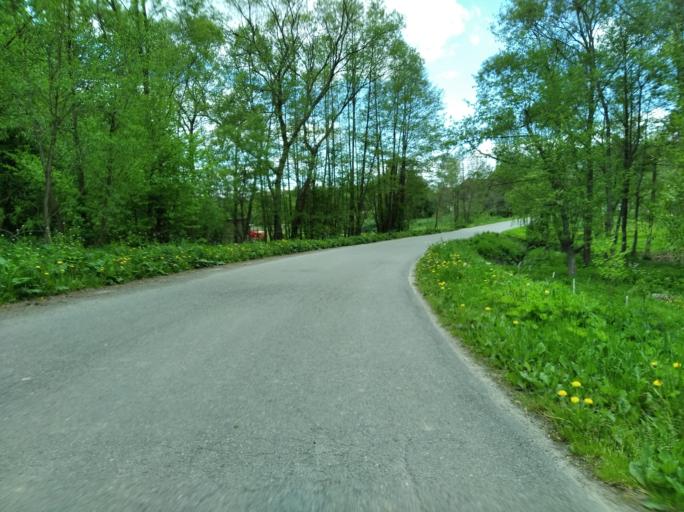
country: PL
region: Subcarpathian Voivodeship
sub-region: Powiat ropczycko-sedziszowski
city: Wielopole Skrzynskie
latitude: 49.9341
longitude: 21.6301
